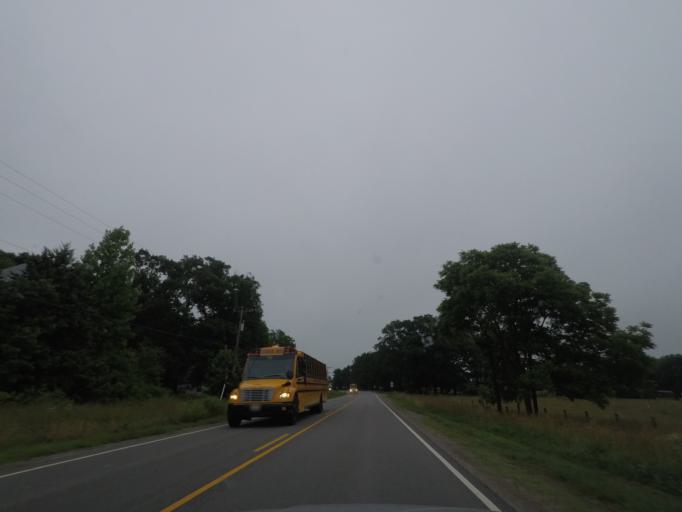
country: US
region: Virginia
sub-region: Fluvanna County
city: Weber City
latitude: 37.6207
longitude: -78.3734
